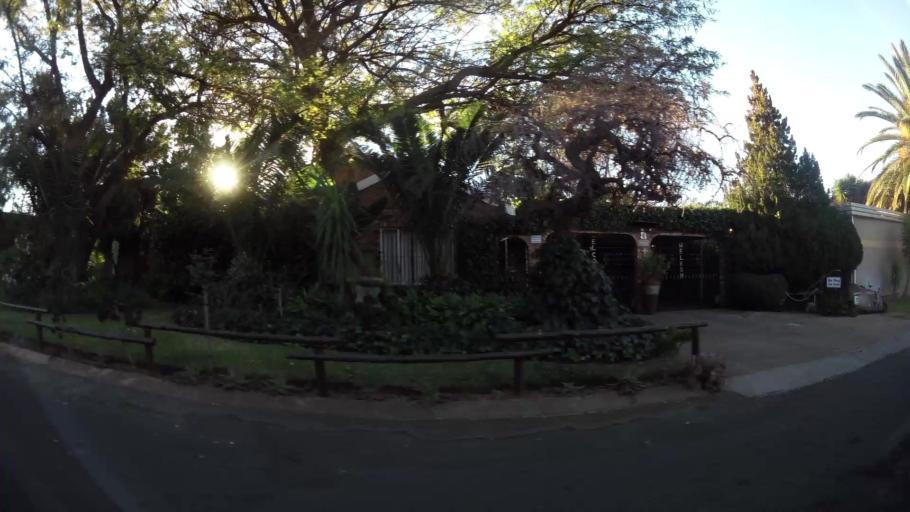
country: ZA
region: Northern Cape
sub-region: Frances Baard District Municipality
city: Kimberley
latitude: -28.7585
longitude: 24.7560
